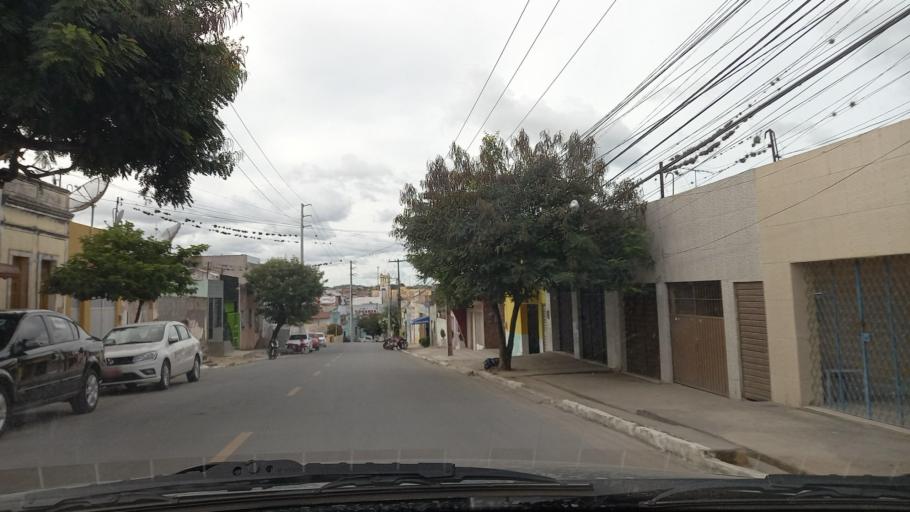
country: BR
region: Pernambuco
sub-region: Gravata
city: Gravata
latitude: -8.2069
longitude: -35.5693
